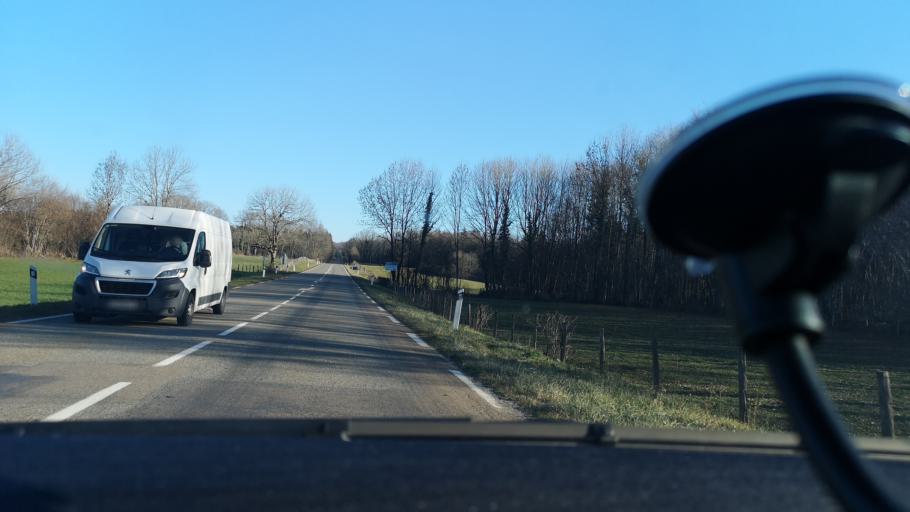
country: FR
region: Franche-Comte
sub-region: Departement du Jura
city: Poligny
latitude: 46.8168
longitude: 5.7506
